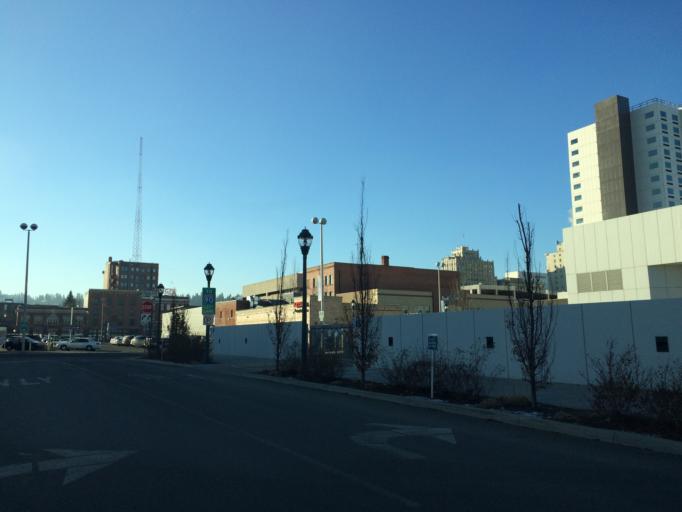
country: US
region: Washington
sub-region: Spokane County
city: Spokane
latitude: 47.6607
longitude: -117.4147
